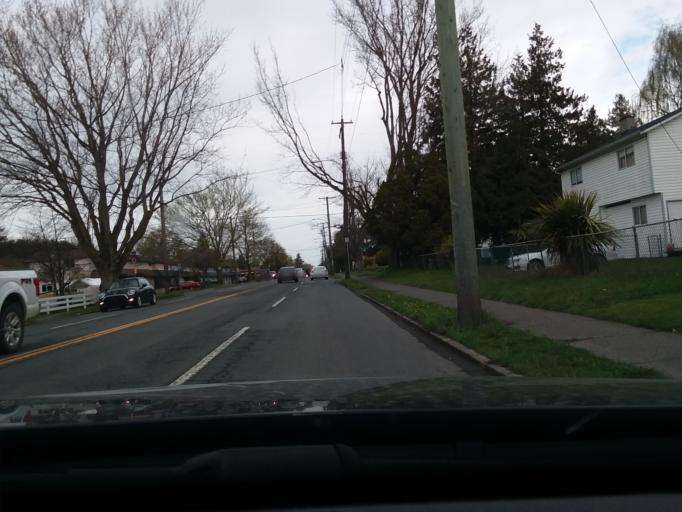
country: CA
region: British Columbia
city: Oak Bay
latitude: 48.4523
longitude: -123.3331
